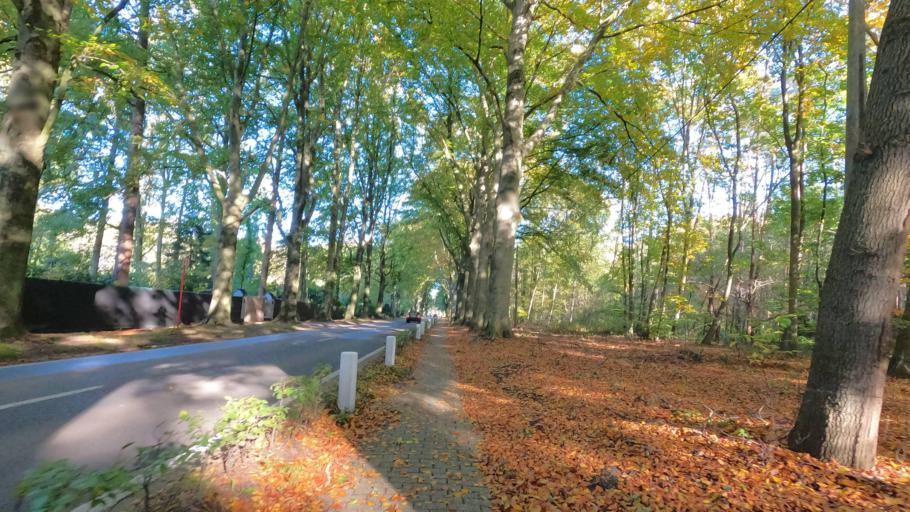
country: BE
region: Flanders
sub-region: Provincie Antwerpen
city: Schilde
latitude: 51.2829
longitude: 4.5705
